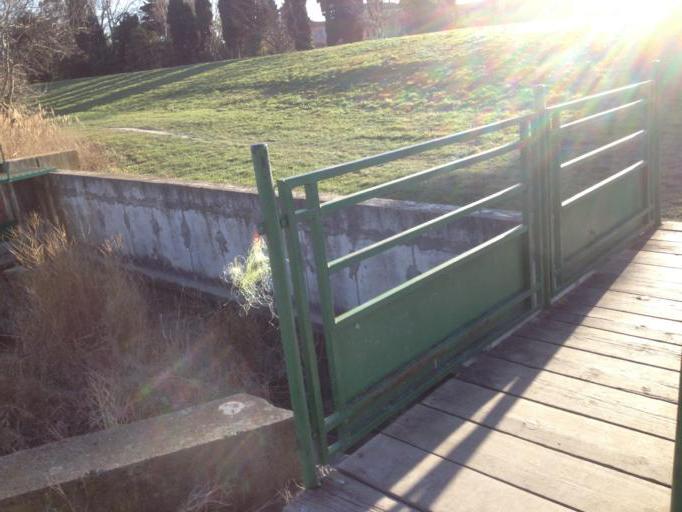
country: FR
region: Provence-Alpes-Cote d'Azur
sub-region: Departement du Vaucluse
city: Orange
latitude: 44.1261
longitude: 4.8309
